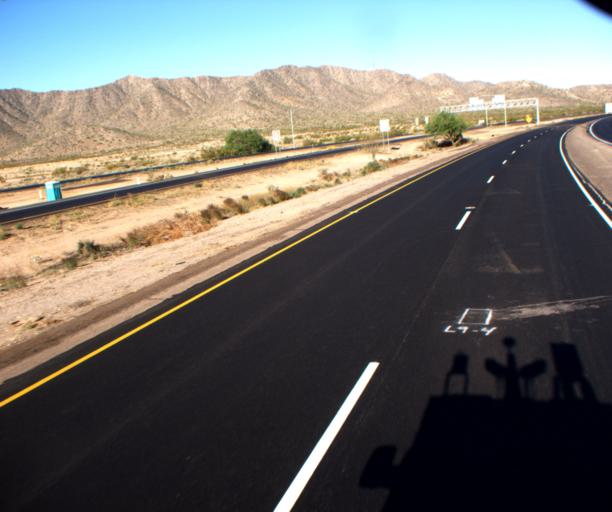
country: US
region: Arizona
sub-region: Pinal County
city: Arizona City
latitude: 32.8199
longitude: -111.6869
